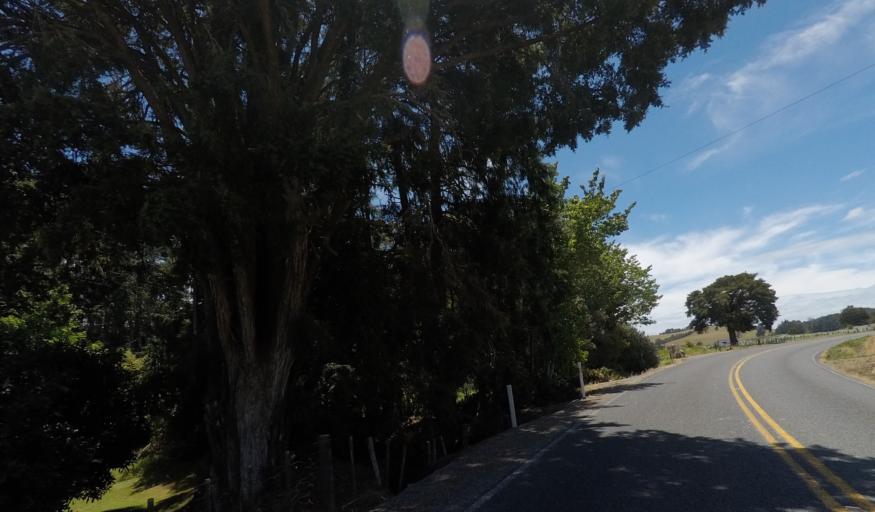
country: NZ
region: Northland
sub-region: Whangarei
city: Whangarei
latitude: -35.5517
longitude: 174.2964
